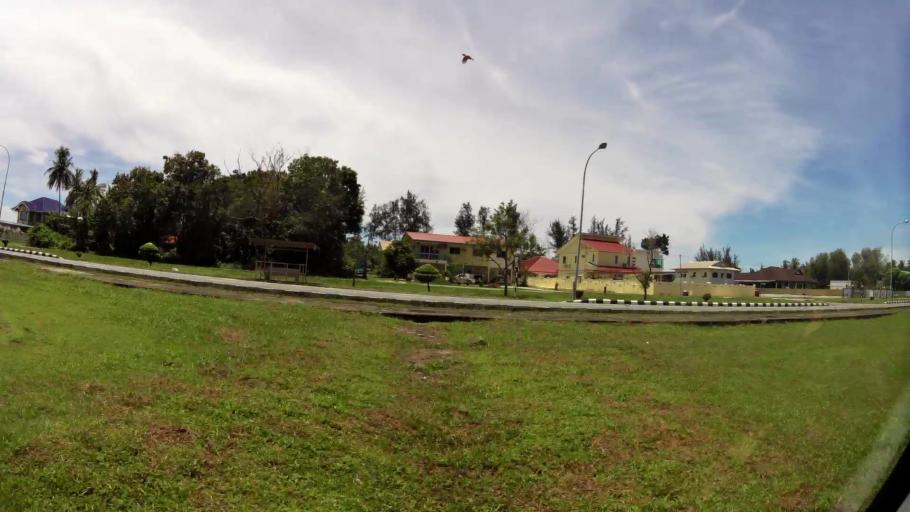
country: BN
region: Belait
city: Kuala Belait
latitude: 4.5932
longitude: 114.2345
